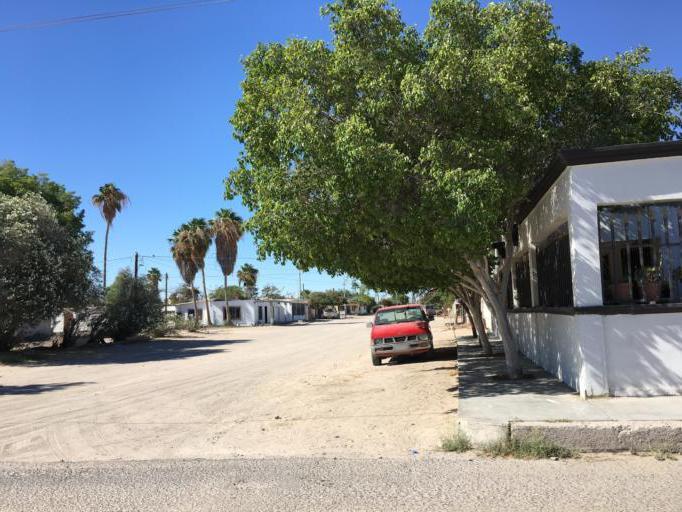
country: MX
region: Sonora
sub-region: Puerto Penasco
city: Puerto Penasco
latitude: 31.3123
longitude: -113.5300
